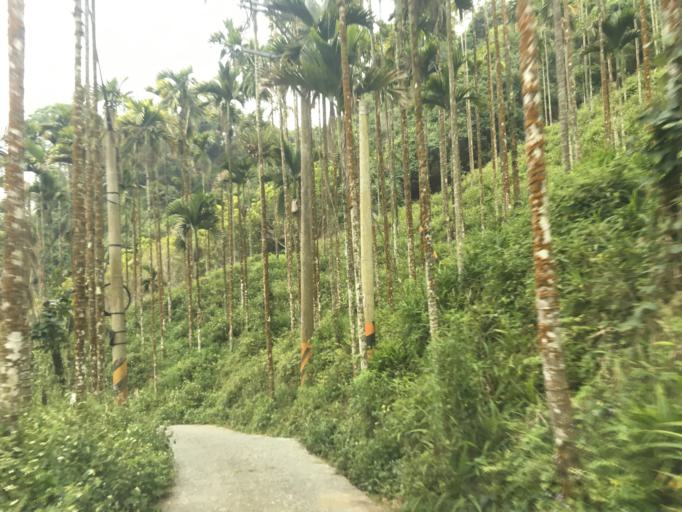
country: TW
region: Taiwan
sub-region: Nantou
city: Puli
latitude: 23.9629
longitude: 120.8409
